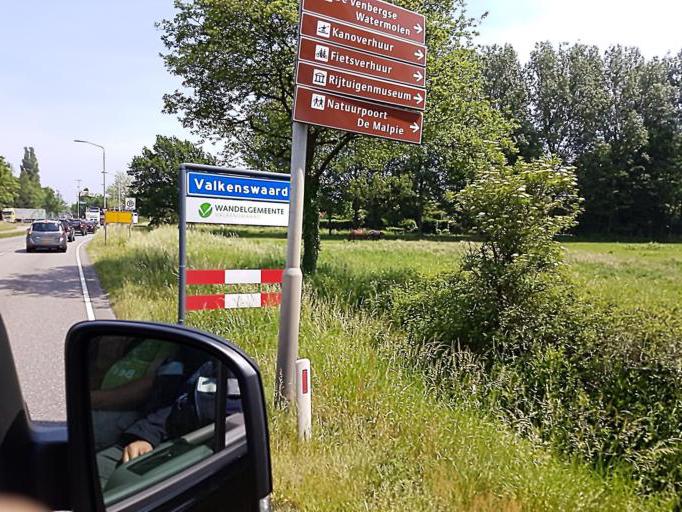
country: NL
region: North Brabant
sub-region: Gemeente Valkenswaard
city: Valkenswaard
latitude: 51.3421
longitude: 5.4474
